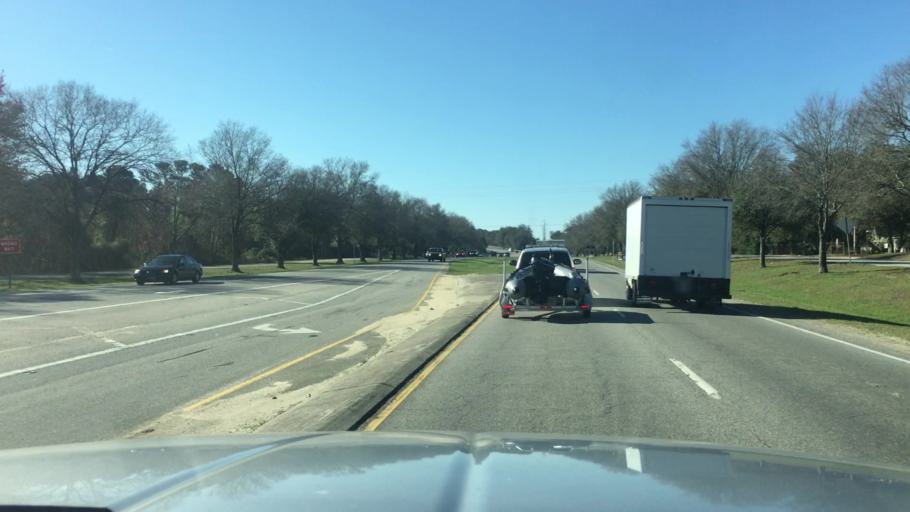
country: US
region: North Carolina
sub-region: New Hanover County
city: Sea Breeze
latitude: 34.0643
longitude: -77.8985
